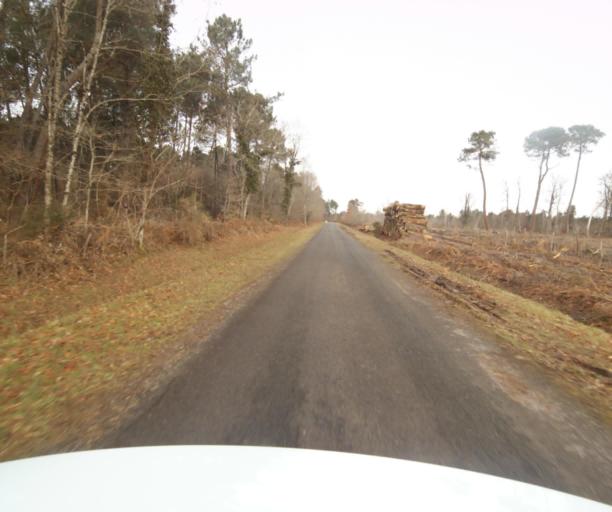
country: FR
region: Aquitaine
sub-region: Departement des Landes
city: Gabarret
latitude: 44.0866
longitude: 0.0708
